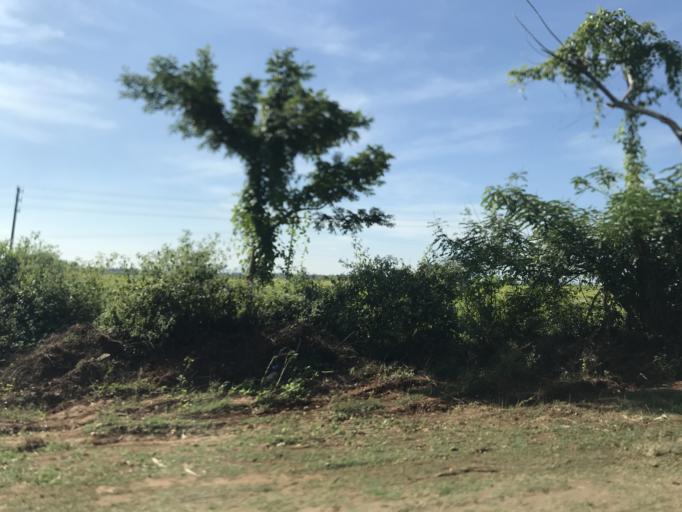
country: IN
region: Karnataka
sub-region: Mysore
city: Heggadadevankote
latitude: 12.1260
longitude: 76.4599
